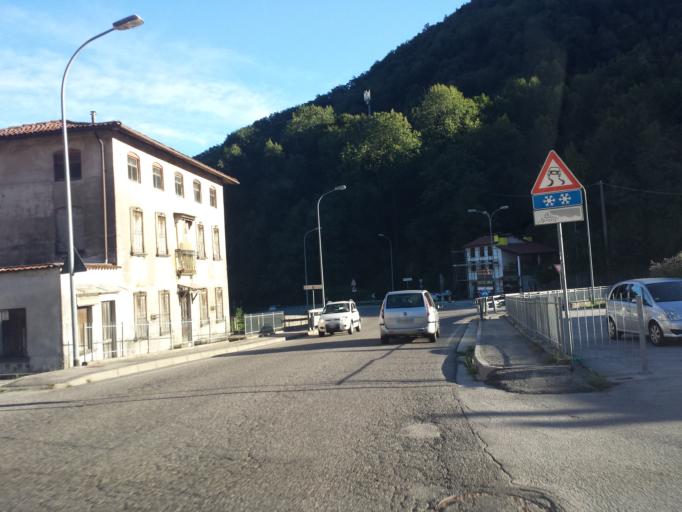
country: IT
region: Veneto
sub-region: Provincia di Vicenza
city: San Quirico
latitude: 45.6755
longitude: 11.2710
